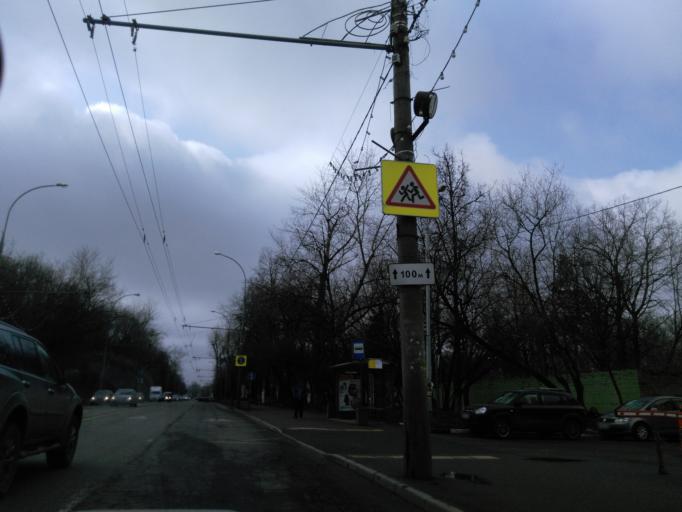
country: RU
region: Moskovskaya
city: Levoberezhnyy
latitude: 55.8406
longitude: 37.4548
